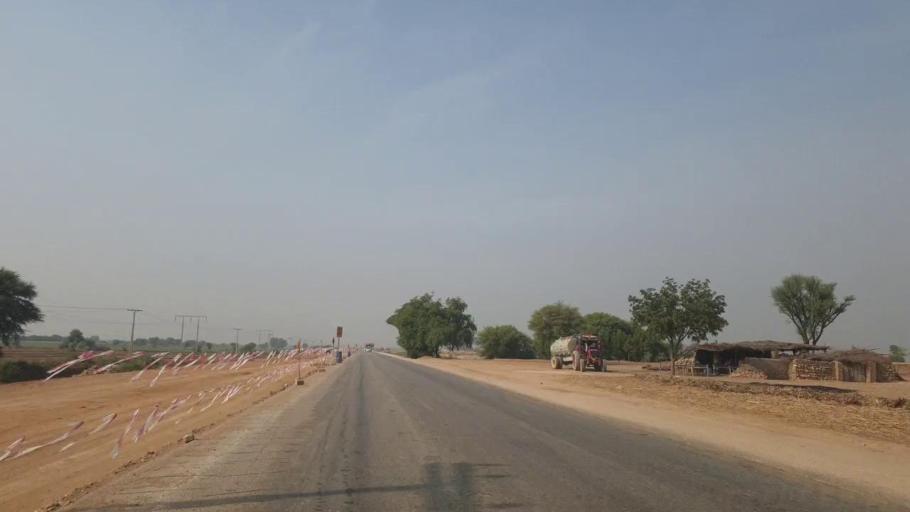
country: PK
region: Sindh
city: Sann
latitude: 26.1340
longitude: 68.0457
